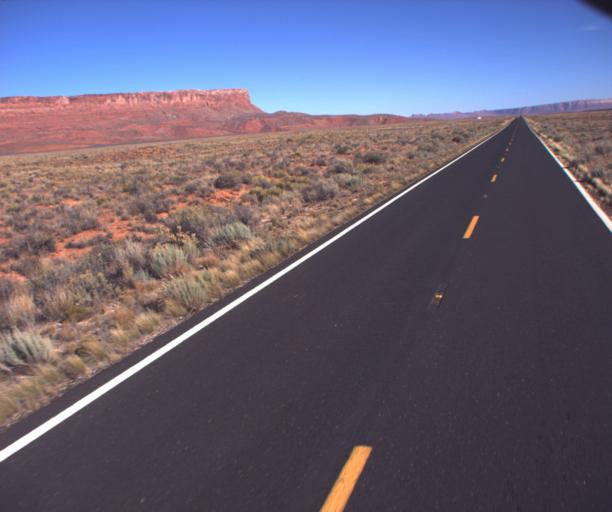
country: US
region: Arizona
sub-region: Coconino County
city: Page
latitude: 36.7001
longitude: -111.9266
